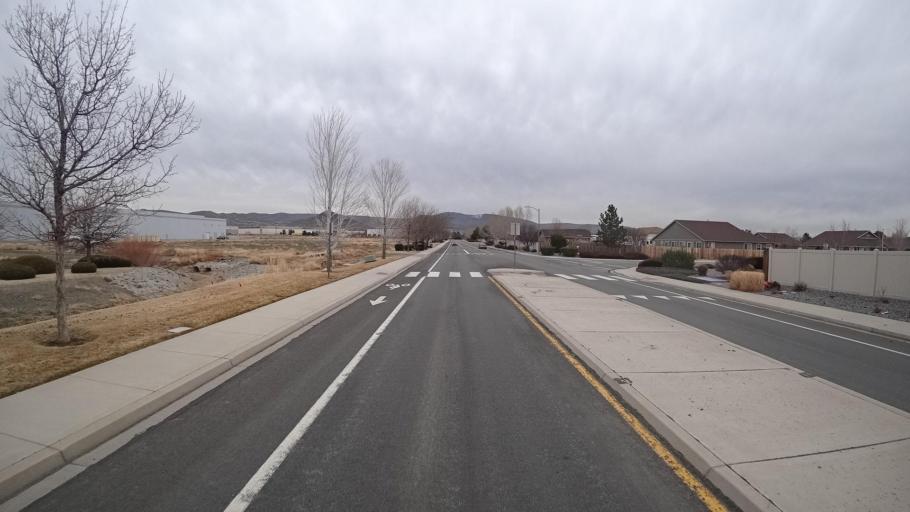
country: US
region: Nevada
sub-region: Washoe County
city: Spanish Springs
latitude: 39.6722
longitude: -119.7134
